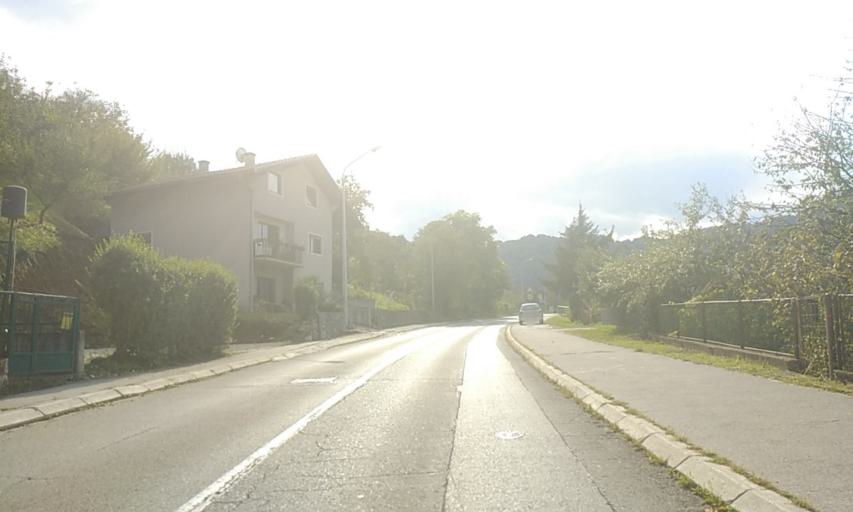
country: BA
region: Republika Srpska
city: Hiseti
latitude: 44.7509
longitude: 17.1656
